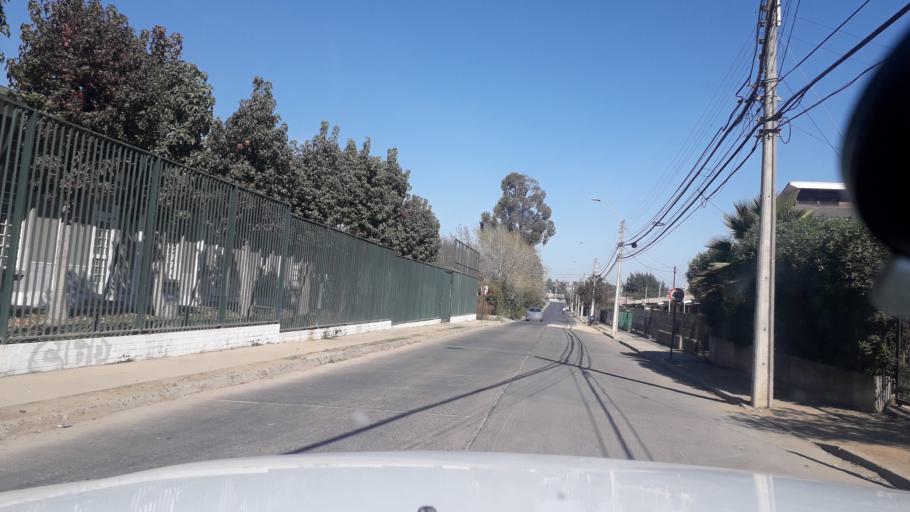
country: CL
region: Valparaiso
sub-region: Provincia de Marga Marga
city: Villa Alemana
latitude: -33.0450
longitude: -71.3487
